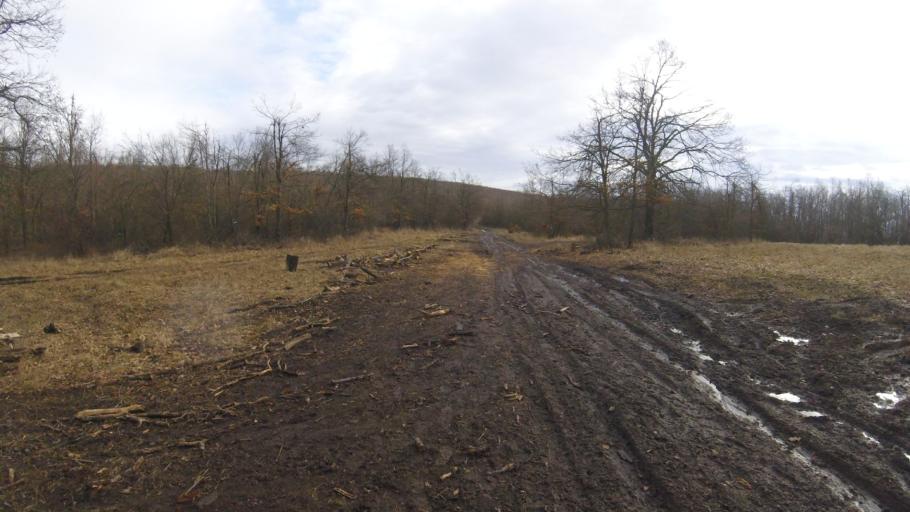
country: HU
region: Pest
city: Pilisszentkereszt
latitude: 47.6979
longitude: 18.9305
